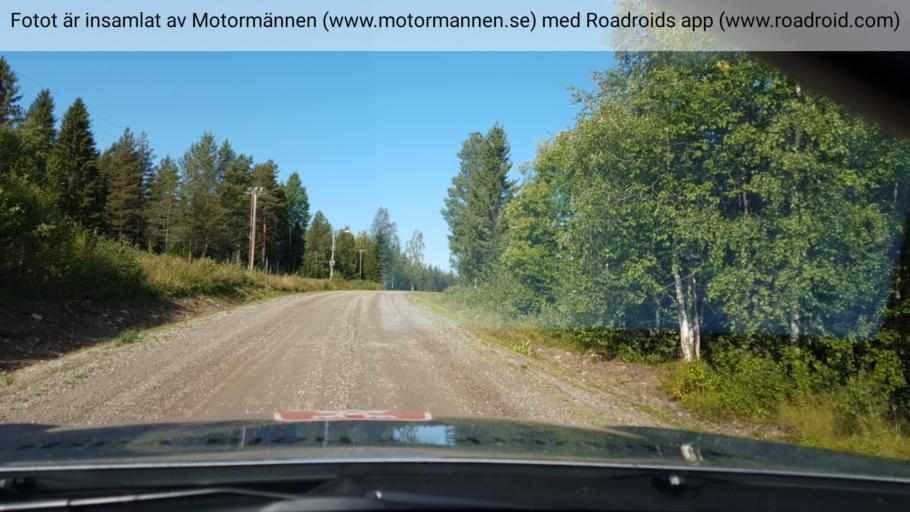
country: SE
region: Norrbotten
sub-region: Kalix Kommun
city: Kalix
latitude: 66.1361
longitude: 23.2334
